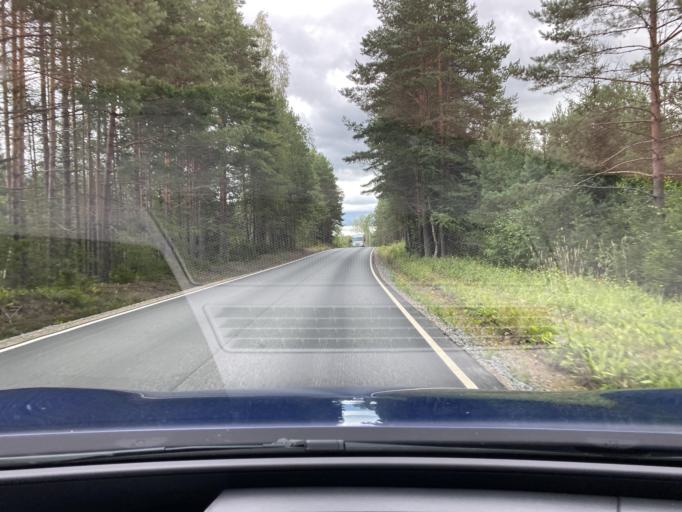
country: FI
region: Pirkanmaa
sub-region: Lounais-Pirkanmaa
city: Vammala
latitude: 61.2845
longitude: 23.0310
